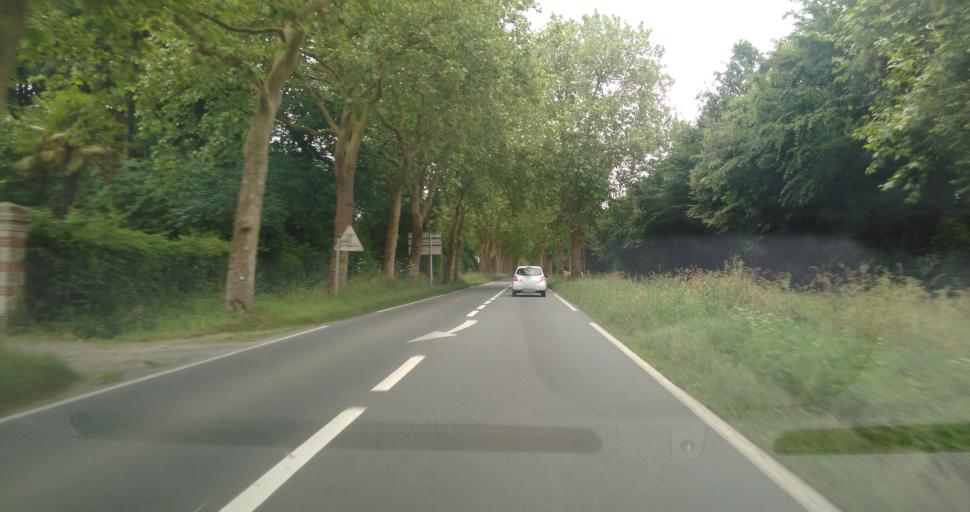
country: FR
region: Pays de la Loire
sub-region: Departement de la Vendee
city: Sainte-Hermine
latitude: 46.5629
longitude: -1.0753
